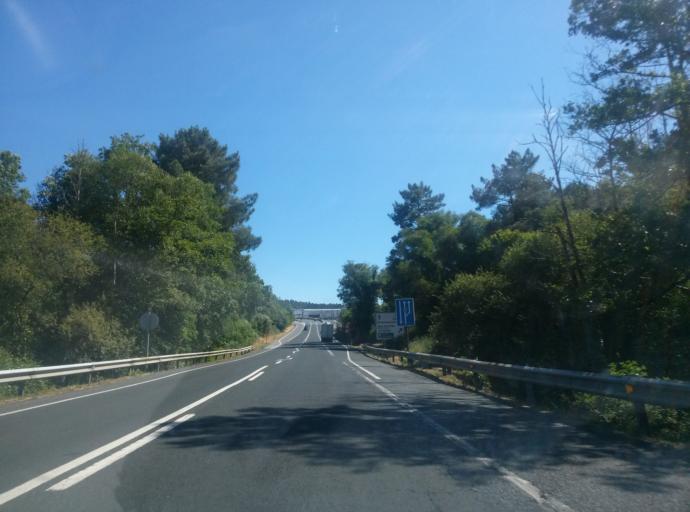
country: ES
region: Galicia
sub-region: Provincia de Lugo
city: Outeiro de Rei
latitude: 43.0664
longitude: -7.6004
